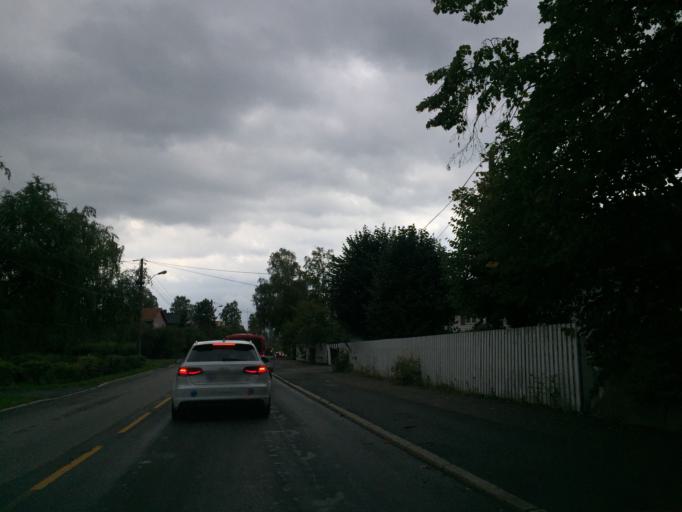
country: NO
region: Oslo
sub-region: Oslo
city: Sjolyststranda
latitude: 59.9411
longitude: 10.6818
